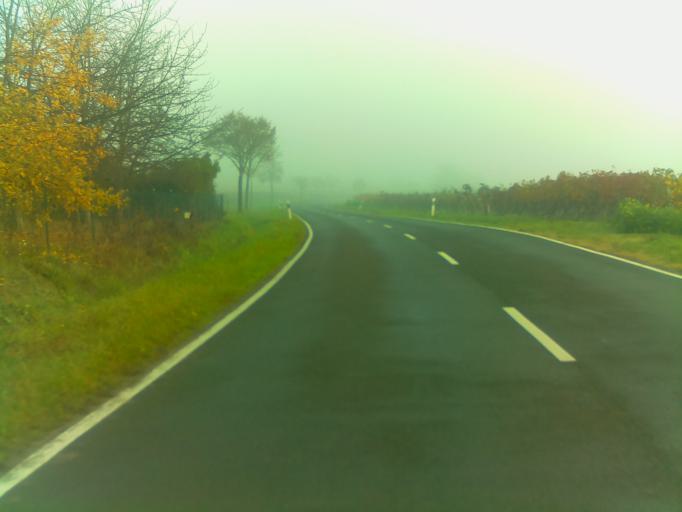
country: DE
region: Rheinland-Pfalz
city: Kallstadt
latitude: 49.4824
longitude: 8.1920
